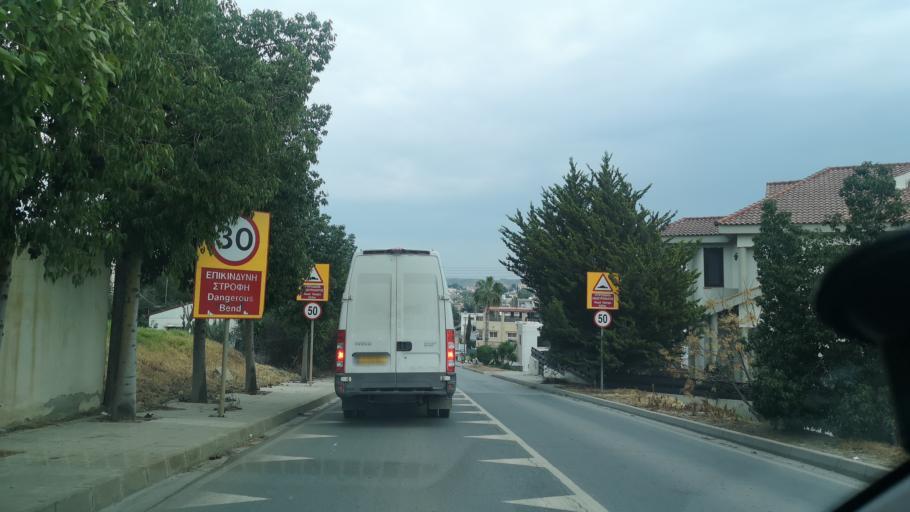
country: CY
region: Lefkosia
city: Tseri
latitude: 35.0755
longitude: 33.3187
